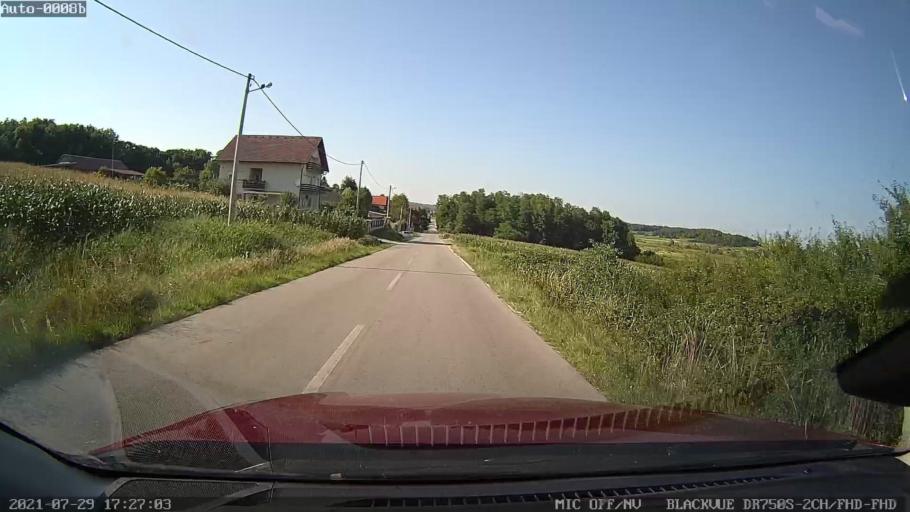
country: HR
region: Varazdinska
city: Ivanec
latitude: 46.2583
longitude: 16.1171
